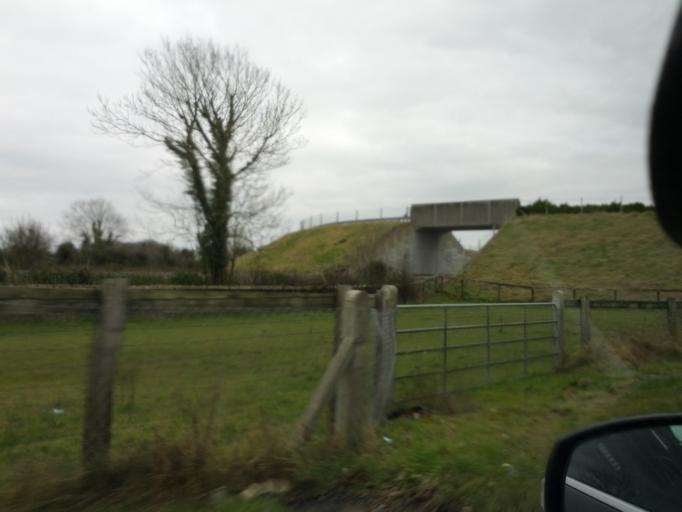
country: IE
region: Connaught
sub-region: County Galway
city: Athenry
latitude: 53.2473
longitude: -8.7484
